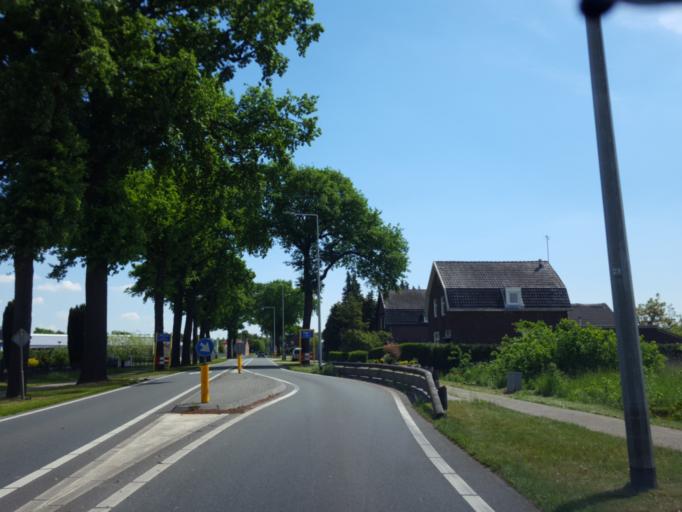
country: NL
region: Limburg
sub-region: Gemeente Weert
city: Weert
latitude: 51.2477
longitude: 5.7409
